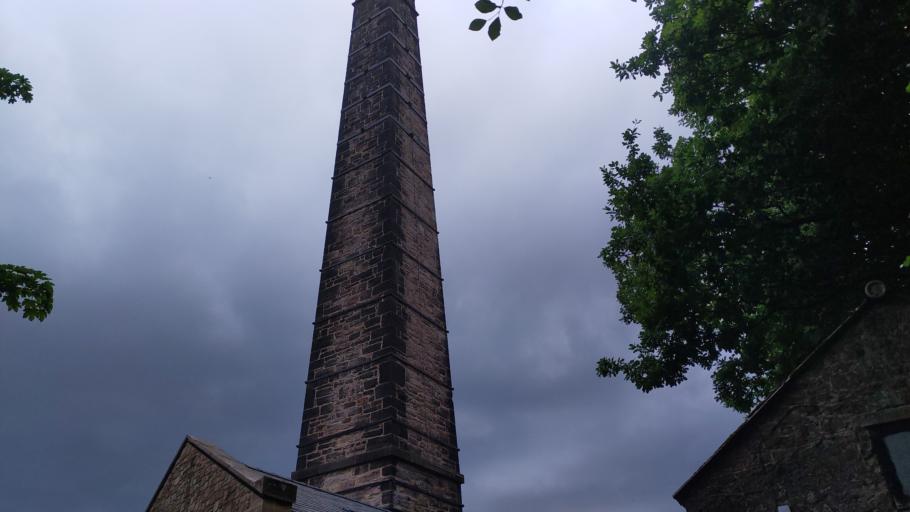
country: GB
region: England
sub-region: Lancashire
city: Chorley
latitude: 53.7034
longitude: -2.5896
